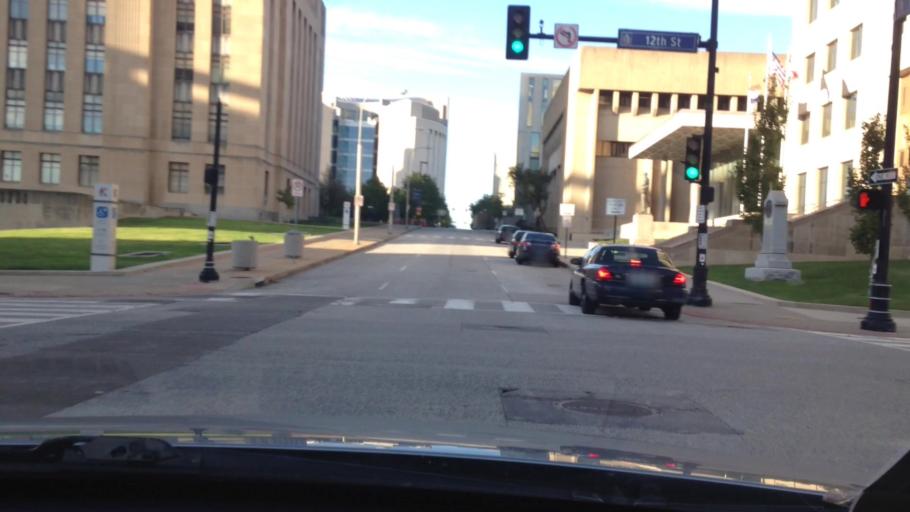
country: US
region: Missouri
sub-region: Jackson County
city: Kansas City
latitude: 39.0996
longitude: -94.5774
